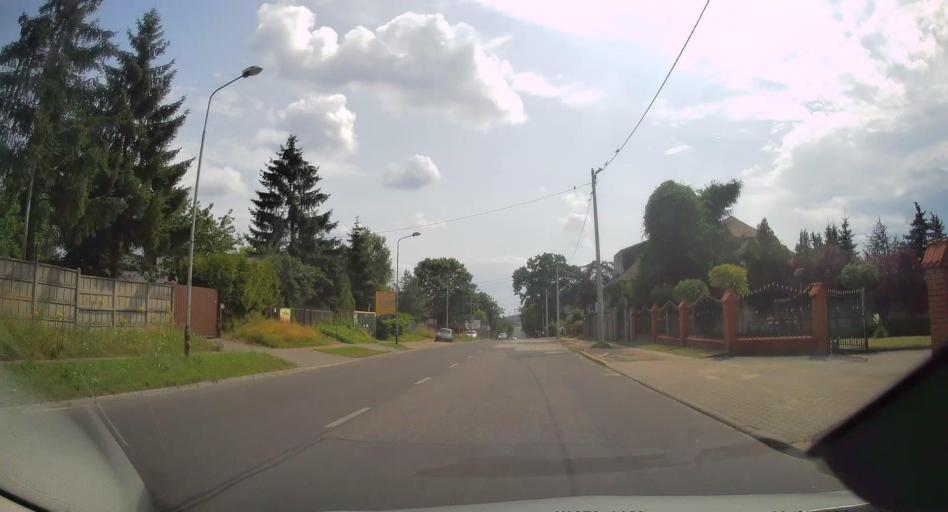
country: PL
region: Silesian Voivodeship
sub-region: Czestochowa
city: Czestochowa
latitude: 50.8110
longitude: 19.0832
